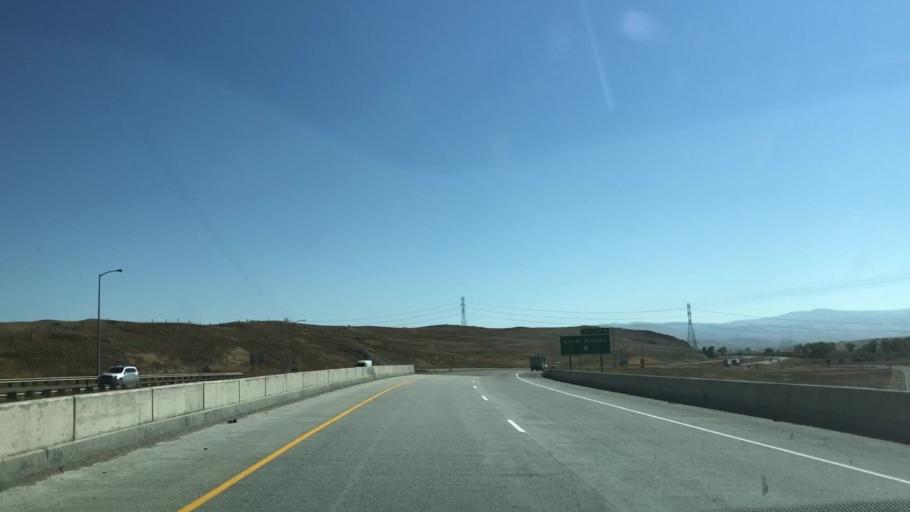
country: US
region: Montana
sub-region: Powell County
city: Deer Lodge
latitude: 46.5096
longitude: -112.7867
